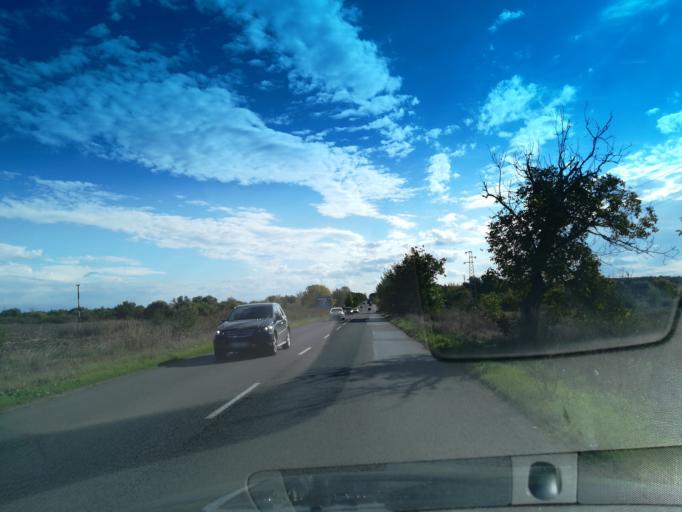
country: BG
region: Stara Zagora
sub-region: Obshtina Stara Zagora
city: Stara Zagora
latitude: 42.3633
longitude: 25.6552
